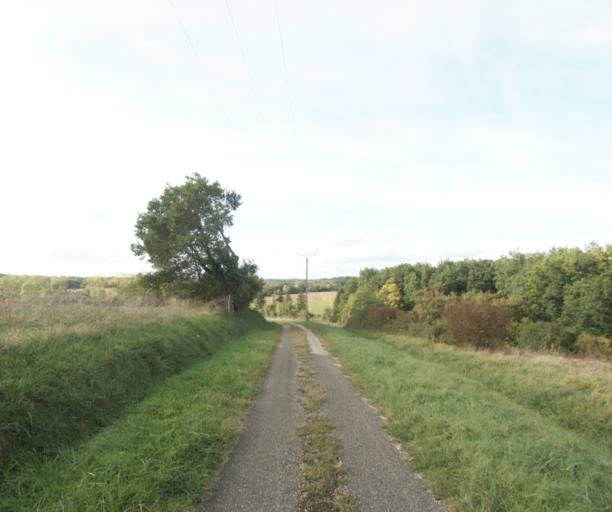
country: FR
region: Midi-Pyrenees
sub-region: Departement du Gers
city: Gondrin
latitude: 43.8712
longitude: 0.2229
